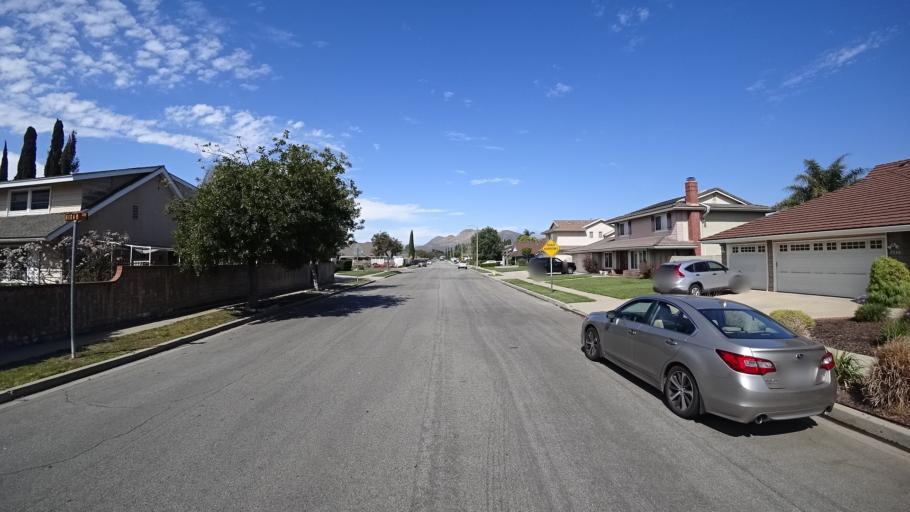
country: US
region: California
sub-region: Ventura County
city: Casa Conejo
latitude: 34.1831
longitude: -118.9345
